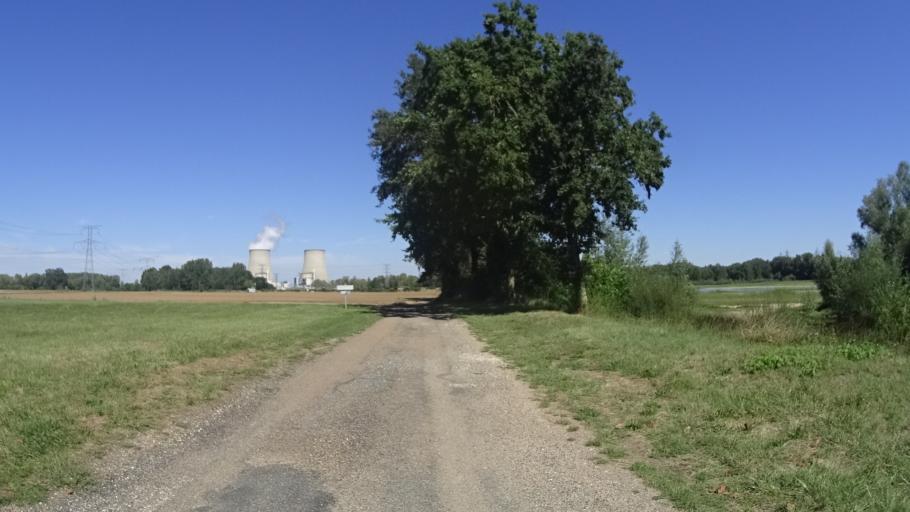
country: FR
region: Bourgogne
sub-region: Departement de la Nievre
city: Neuvy-sur-Loire
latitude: 47.4954
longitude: 2.8896
